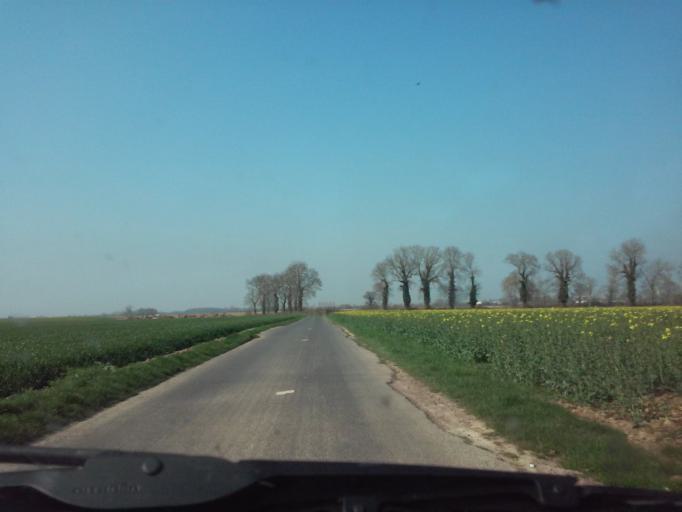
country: FR
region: Lower Normandy
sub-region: Departement du Calvados
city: Cheux
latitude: 49.1983
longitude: -0.5465
